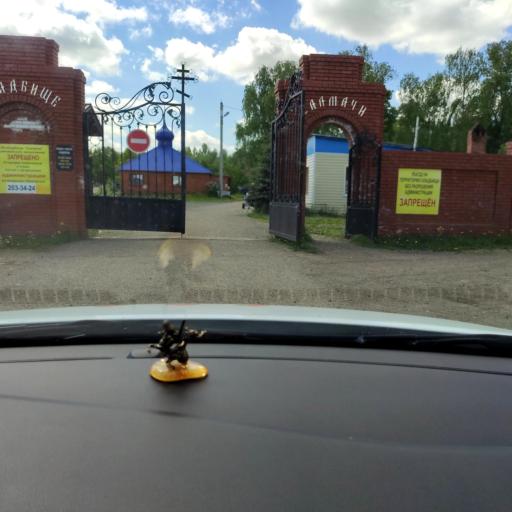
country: RU
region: Tatarstan
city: Stolbishchi
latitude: 55.7369
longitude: 49.2796
